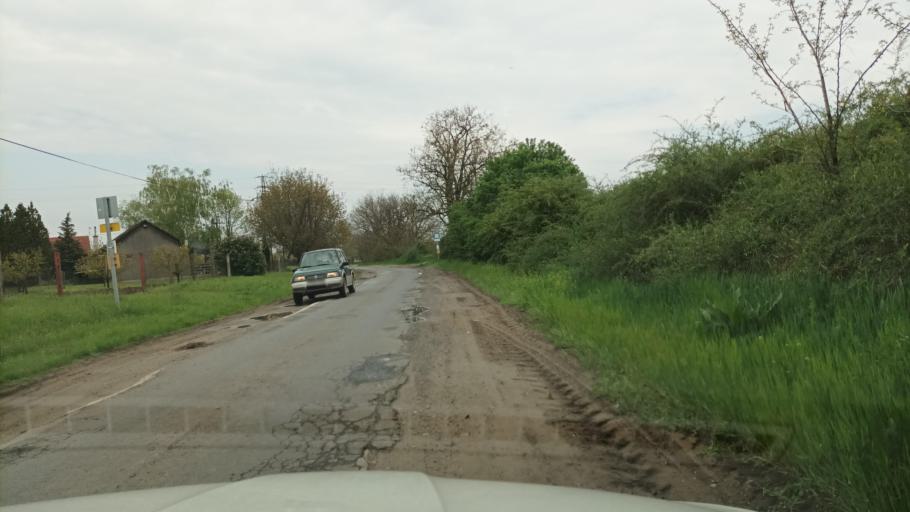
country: HU
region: Pest
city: Nagykoros
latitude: 47.0132
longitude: 19.7942
